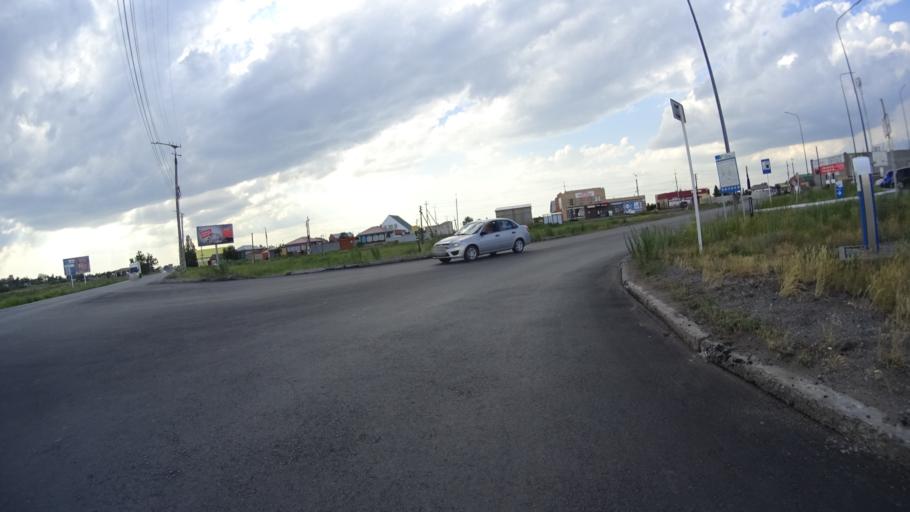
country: RU
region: Chelyabinsk
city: Troitsk
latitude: 54.0823
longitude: 61.5188
